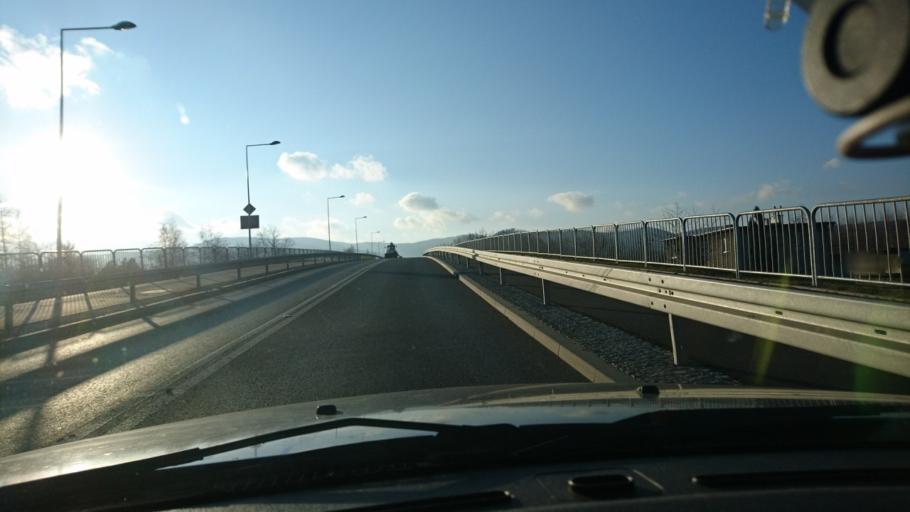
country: PL
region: Silesian Voivodeship
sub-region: Powiat bielski
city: Jaworze
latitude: 49.8125
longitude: 18.9750
